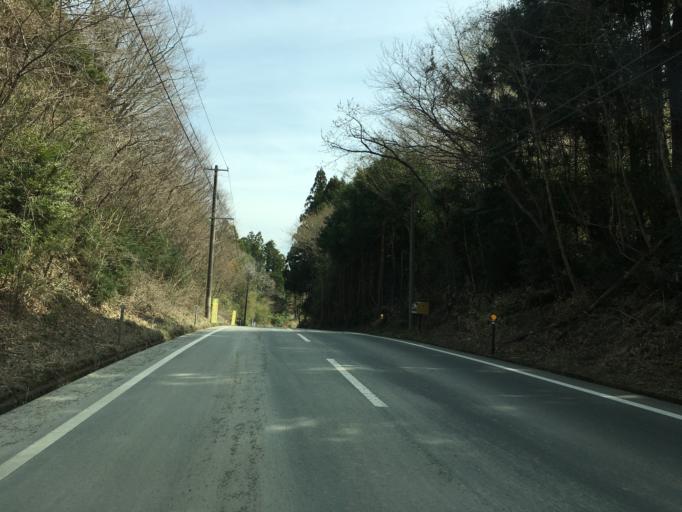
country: JP
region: Fukushima
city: Namie
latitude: 37.4558
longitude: 140.9742
